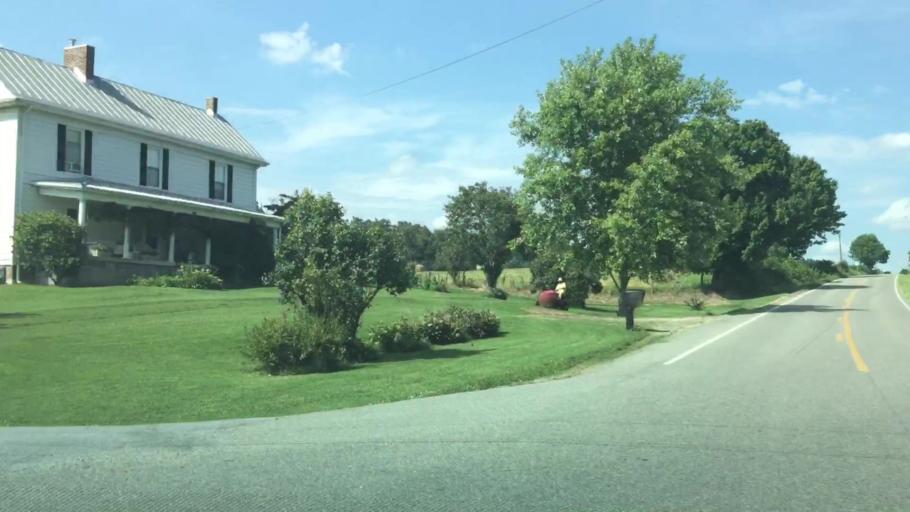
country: US
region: Tennessee
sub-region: Sullivan County
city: Fairmount
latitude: 36.5907
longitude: -82.0493
